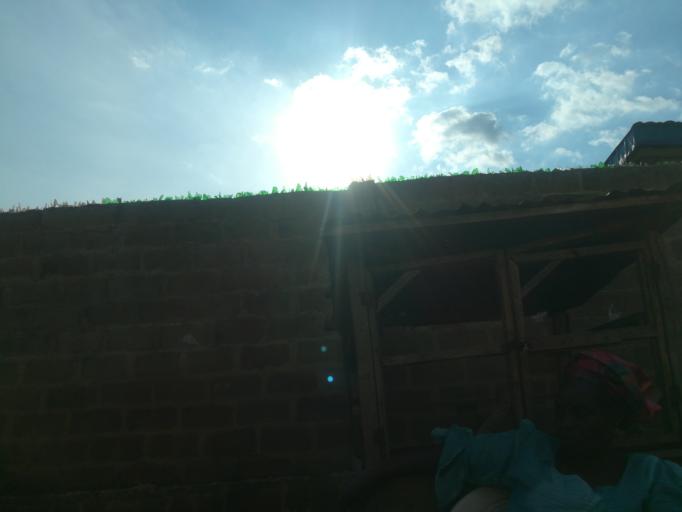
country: NG
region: Oyo
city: Ibadan
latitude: 7.3909
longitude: 3.8794
